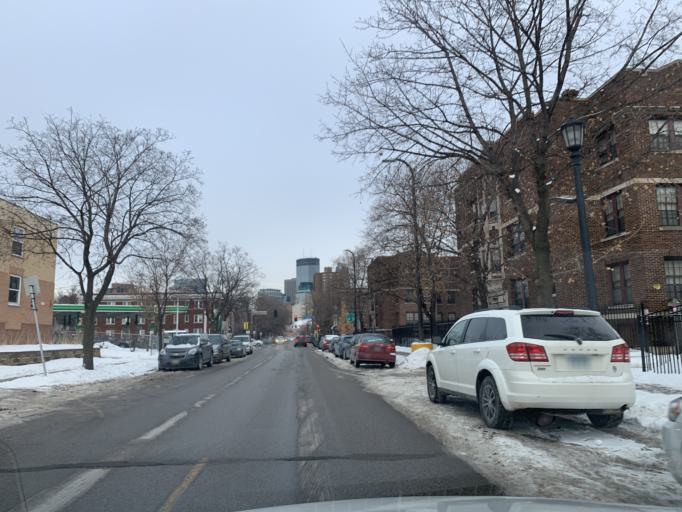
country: US
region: Minnesota
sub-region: Hennepin County
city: Minneapolis
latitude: 44.9617
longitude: -93.2727
